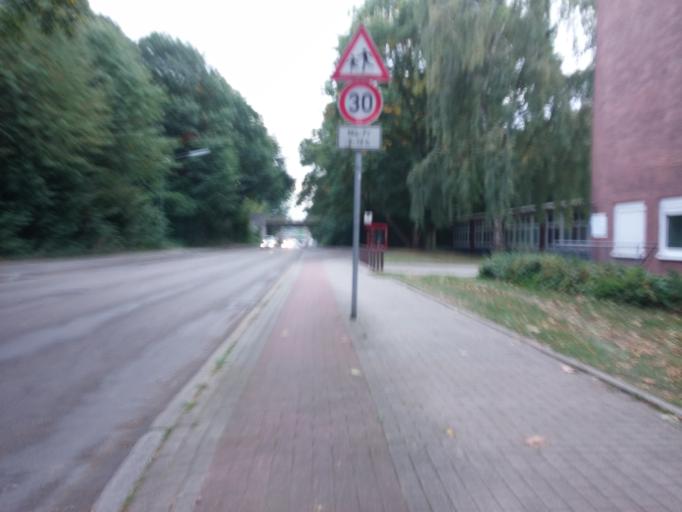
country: DE
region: North Rhine-Westphalia
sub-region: Regierungsbezirk Munster
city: Gladbeck
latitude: 51.6033
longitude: 7.0422
